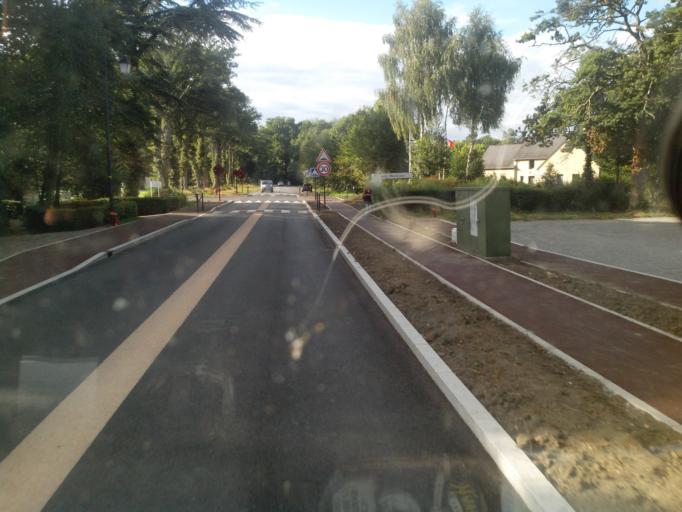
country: FR
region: Brittany
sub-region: Departement d'Ille-et-Vilaine
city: Paimpont
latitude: 48.0235
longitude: -2.1724
